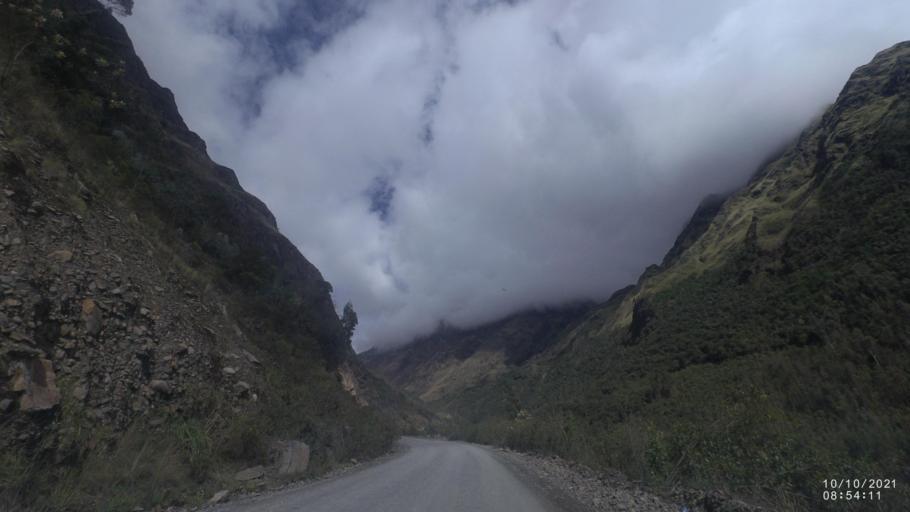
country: BO
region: La Paz
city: Quime
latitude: -16.9886
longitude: -67.2326
